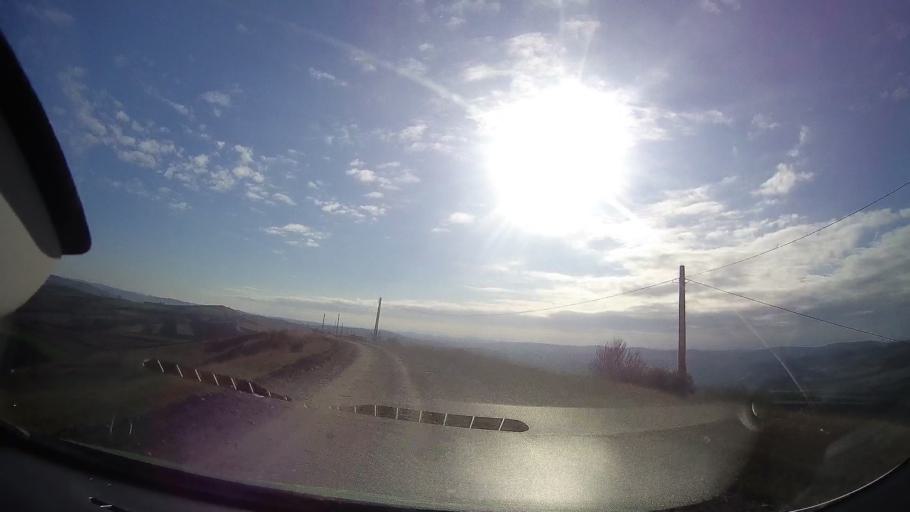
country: RO
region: Mures
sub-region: Comuna Saulia
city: Saulia
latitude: 46.5910
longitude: 24.2201
